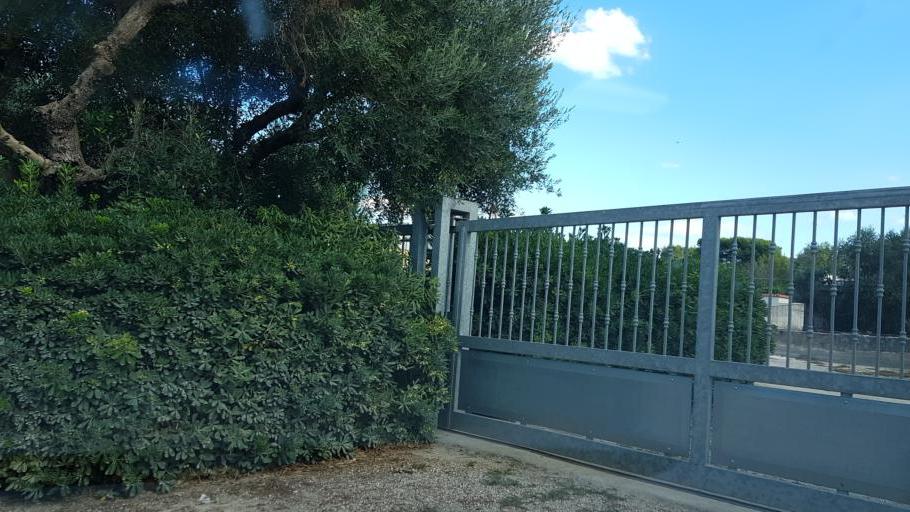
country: IT
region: Apulia
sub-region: Provincia di Lecce
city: Nardo
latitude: 40.1556
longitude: 18.0172
